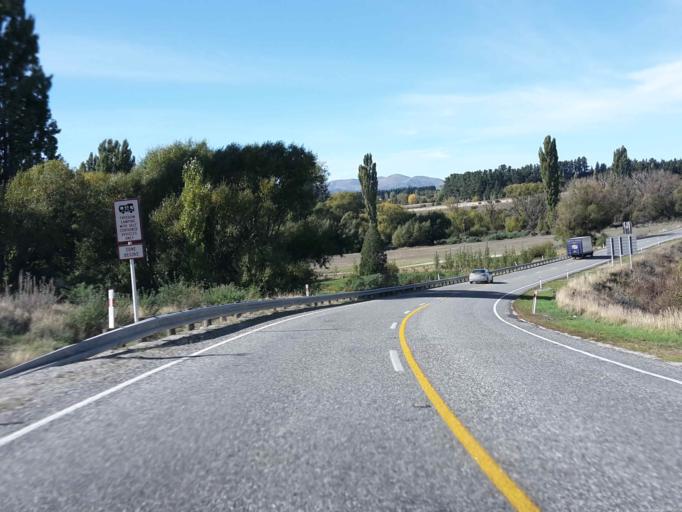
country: NZ
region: Otago
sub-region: Queenstown-Lakes District
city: Wanaka
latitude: -44.6969
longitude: 169.1739
